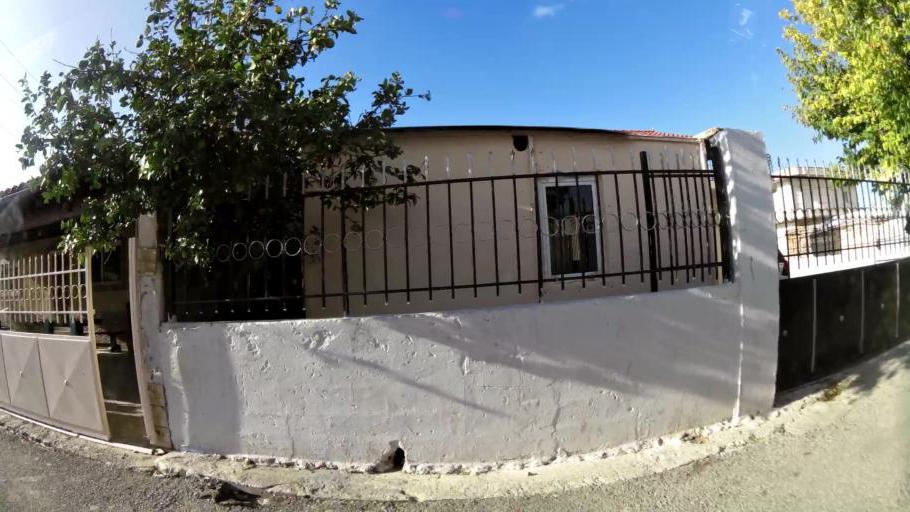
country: GR
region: Attica
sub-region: Nomarchia Anatolikis Attikis
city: Acharnes
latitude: 38.0758
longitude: 23.7482
